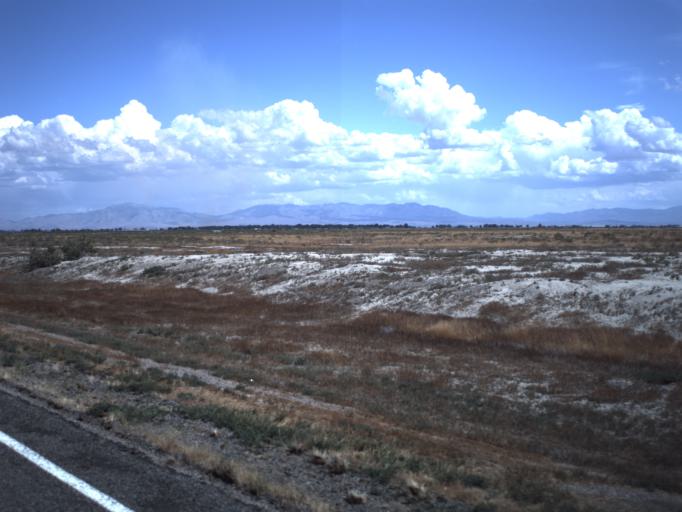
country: US
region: Utah
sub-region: Millard County
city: Delta
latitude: 39.3263
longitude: -112.7294
